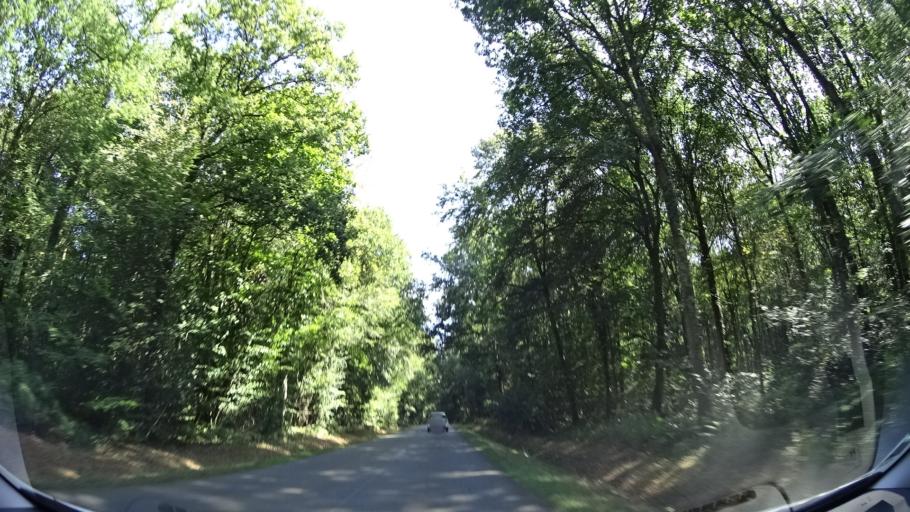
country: FR
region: Brittany
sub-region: Departement d'Ille-et-Vilaine
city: Saint-Sulpice-la-Foret
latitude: 48.2102
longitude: -1.5536
